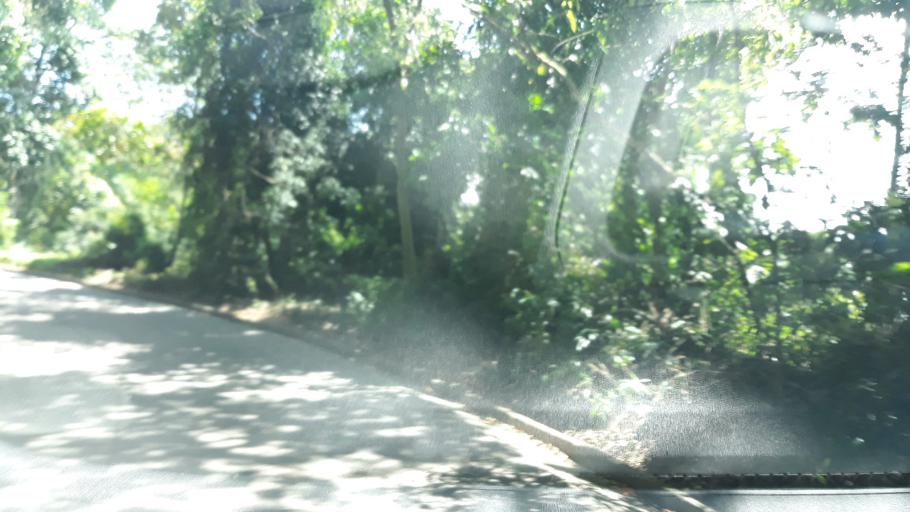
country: BR
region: Rio de Janeiro
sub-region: Rio De Janeiro
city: Rio de Janeiro
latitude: -22.9478
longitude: -43.2138
